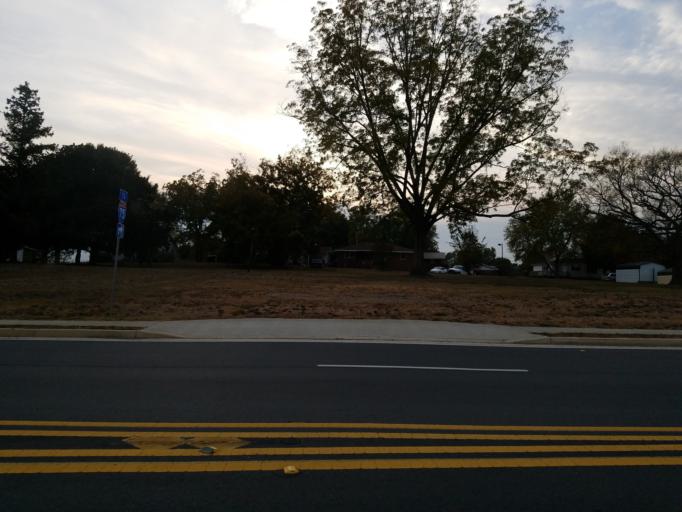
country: US
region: Georgia
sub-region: Gordon County
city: Calhoun
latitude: 34.5797
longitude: -84.9431
